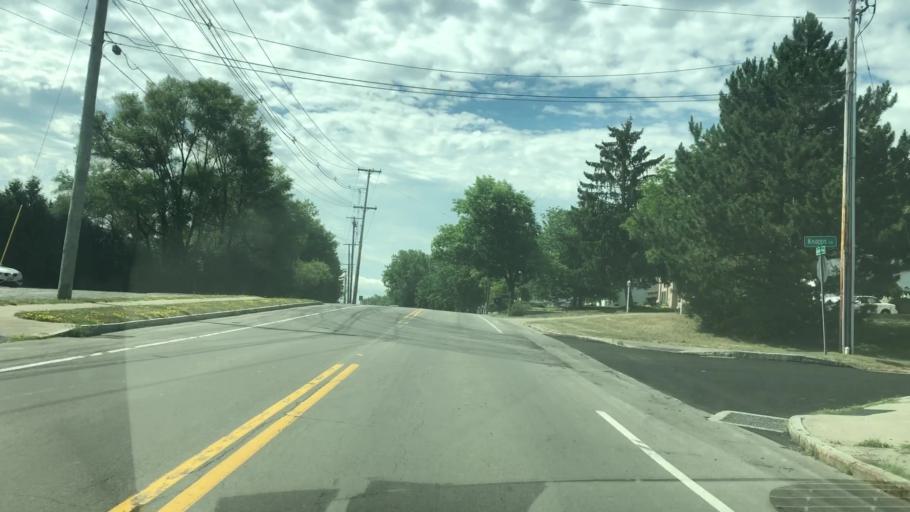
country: US
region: New York
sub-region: Monroe County
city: Fairport
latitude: 43.0858
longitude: -77.4022
